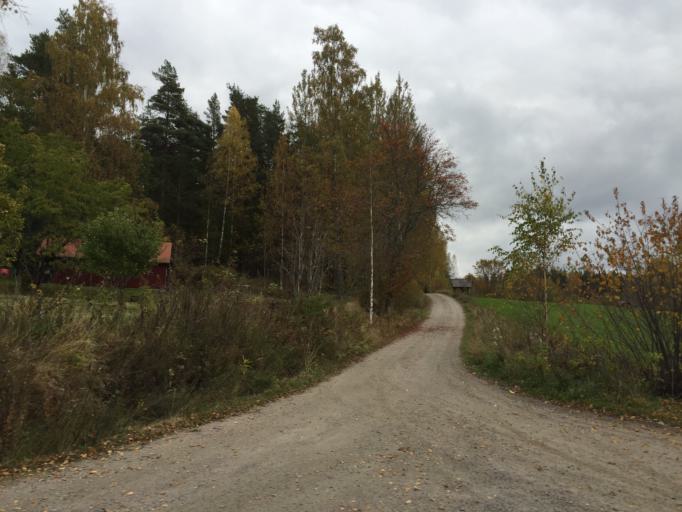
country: SE
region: Soedermanland
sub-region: Vingakers Kommun
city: Vingaker
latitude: 59.0352
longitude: 15.7848
